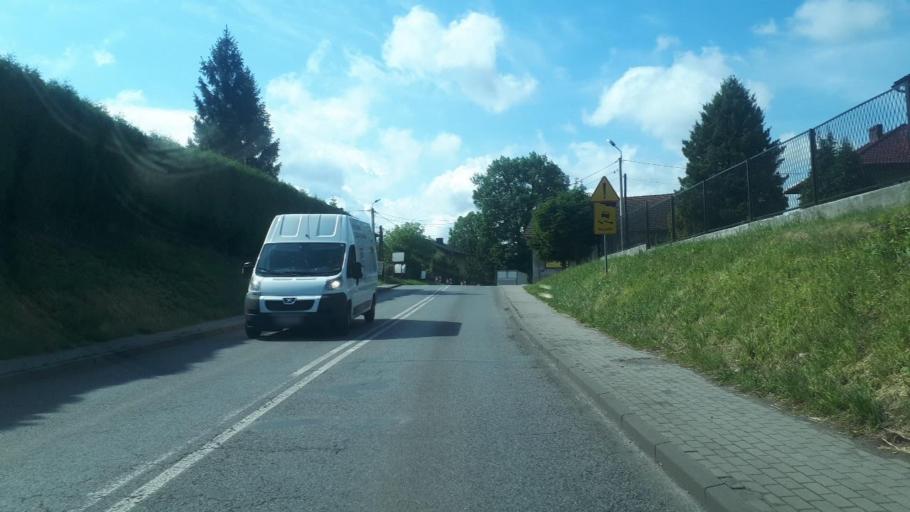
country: PL
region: Lesser Poland Voivodeship
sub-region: Powiat oswiecimski
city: Brzeszcze
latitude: 49.9600
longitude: 19.1391
